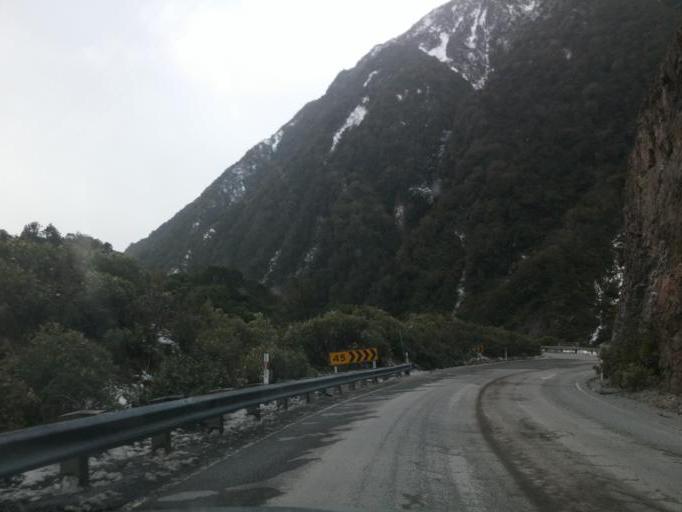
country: NZ
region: West Coast
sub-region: Grey District
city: Greymouth
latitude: -42.8815
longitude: 171.5549
